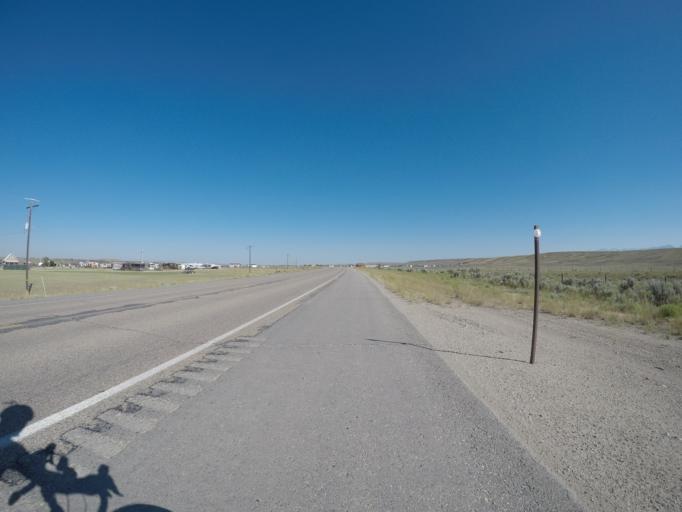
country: US
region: Wyoming
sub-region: Sublette County
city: Pinedale
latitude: 42.7594
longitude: -109.7331
